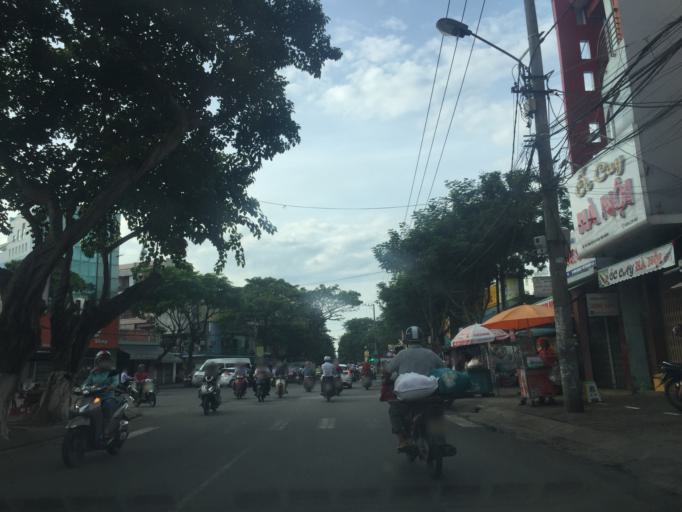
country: VN
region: Da Nang
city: Da Nang
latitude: 16.0728
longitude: 108.2130
